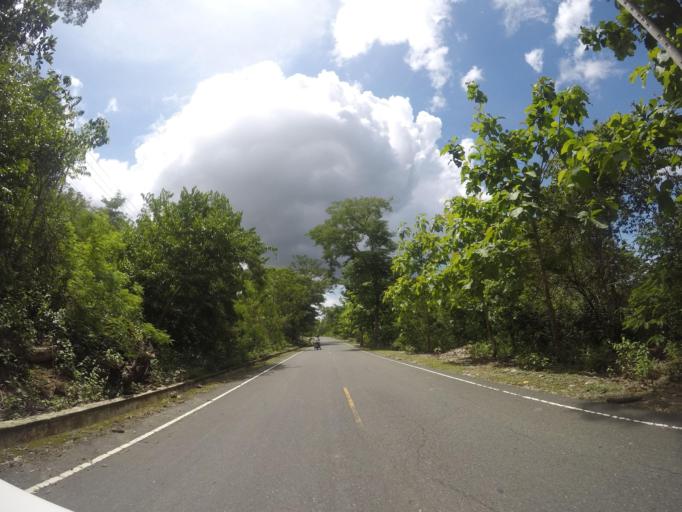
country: TL
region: Bobonaro
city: Maliana
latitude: -8.9472
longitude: 125.0973
